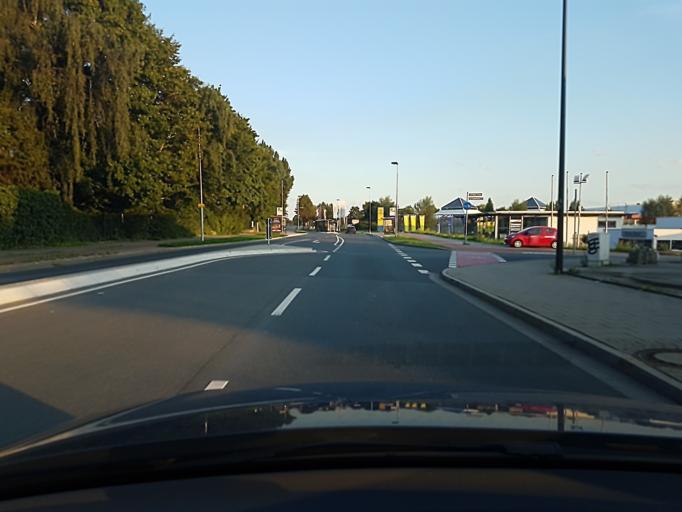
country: DE
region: North Rhine-Westphalia
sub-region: Regierungsbezirk Dusseldorf
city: Erkrath
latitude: 51.2265
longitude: 6.8581
